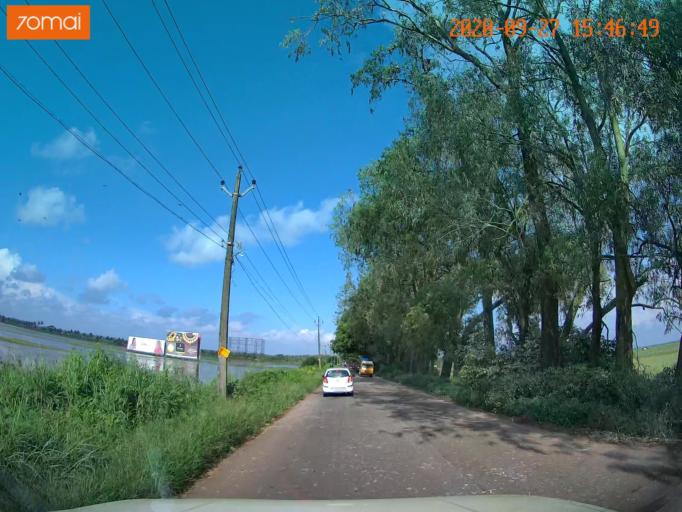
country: IN
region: Kerala
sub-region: Thrissur District
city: Thanniyam
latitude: 10.4810
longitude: 76.1245
